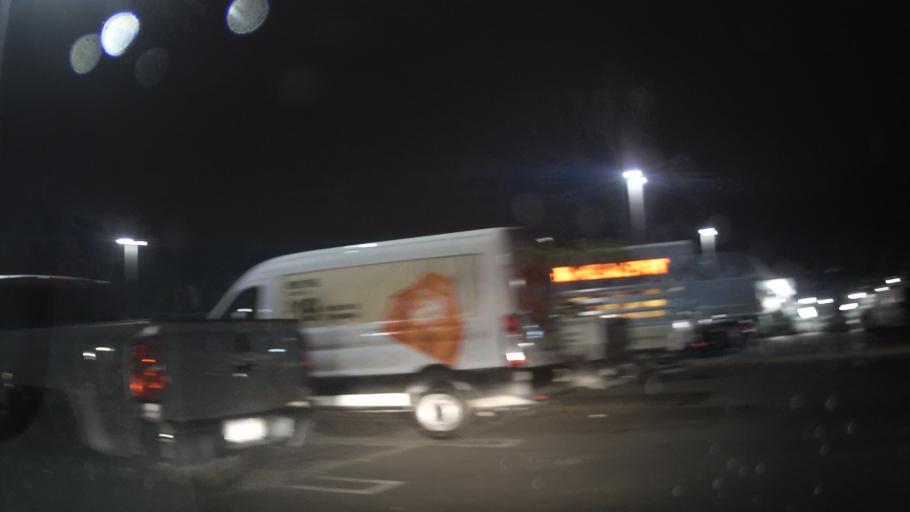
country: US
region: California
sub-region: San Diego County
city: Poway
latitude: 32.9834
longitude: -117.0744
